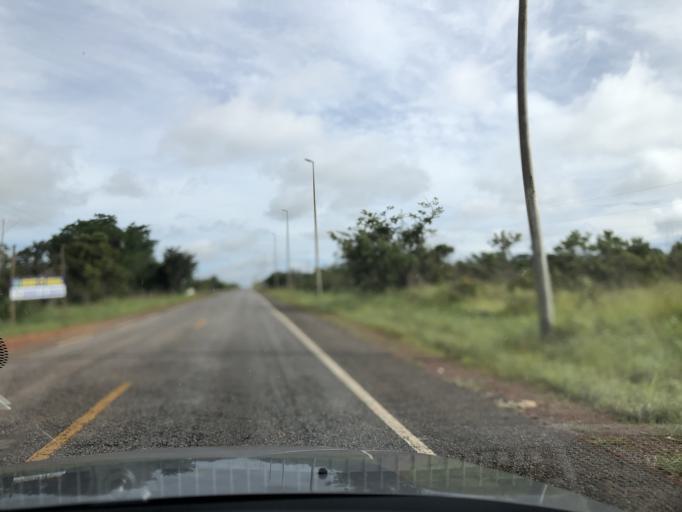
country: BR
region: Federal District
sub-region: Brasilia
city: Brasilia
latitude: -15.7077
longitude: -48.0877
